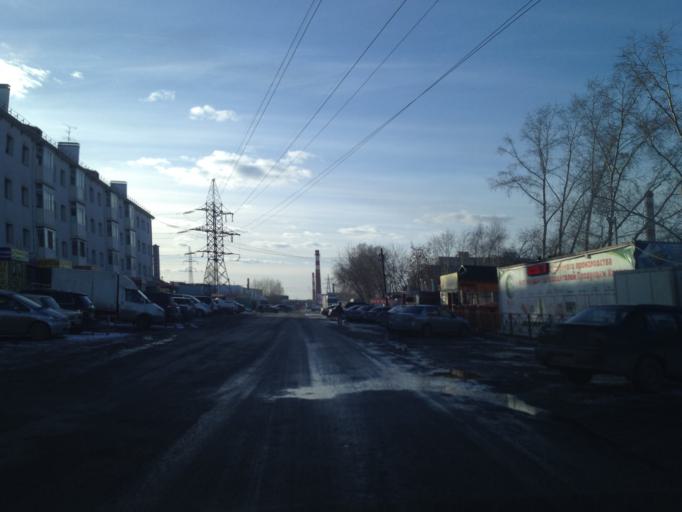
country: RU
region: Sverdlovsk
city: Yekaterinburg
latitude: 56.8621
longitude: 60.5365
